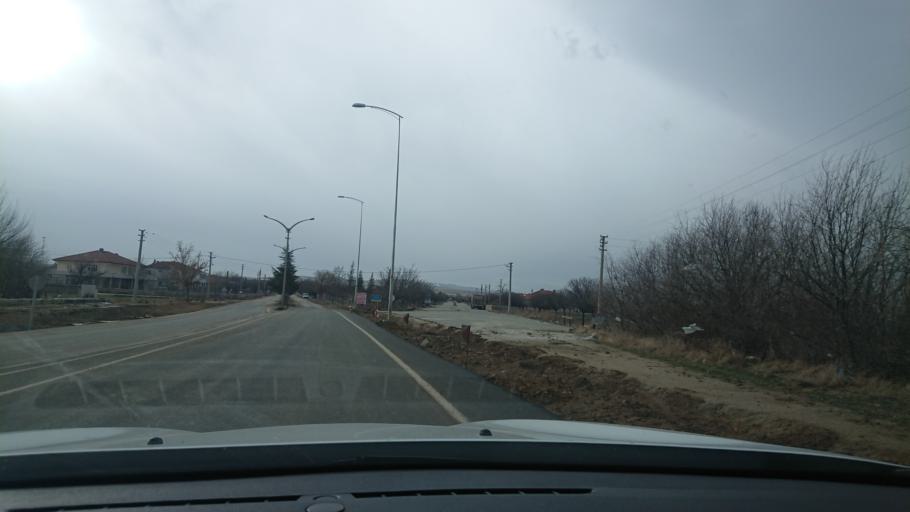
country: TR
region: Aksaray
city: Agacoren
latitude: 38.9314
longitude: 33.9677
